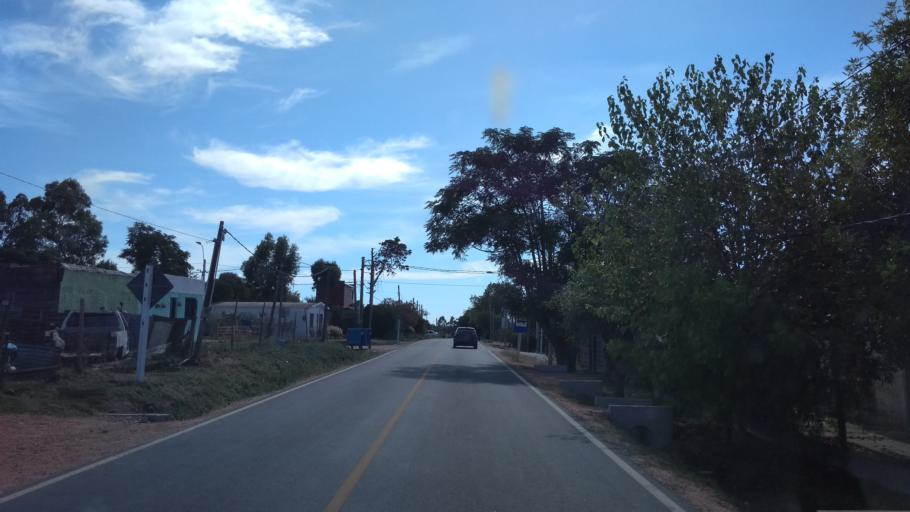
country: UY
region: Canelones
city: Joaquin Suarez
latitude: -34.7294
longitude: -56.0304
